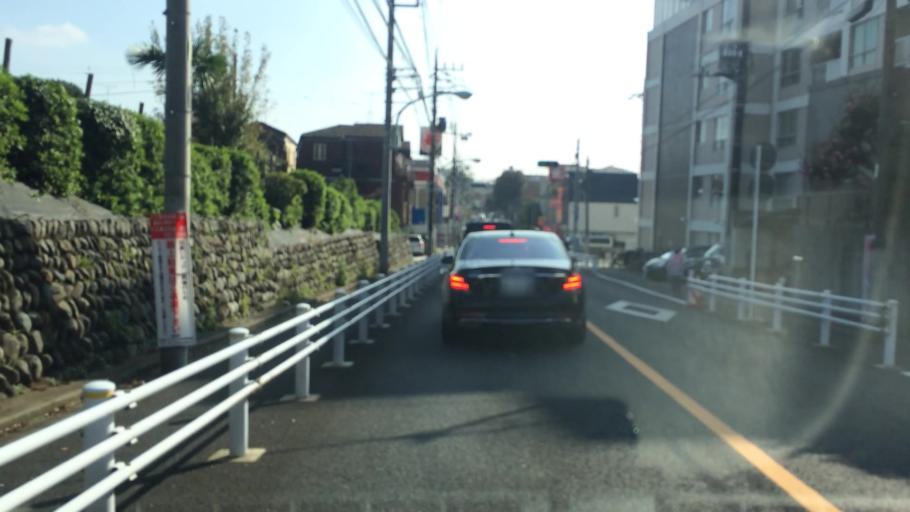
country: JP
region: Tokyo
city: Tokyo
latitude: 35.6228
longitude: 139.6665
